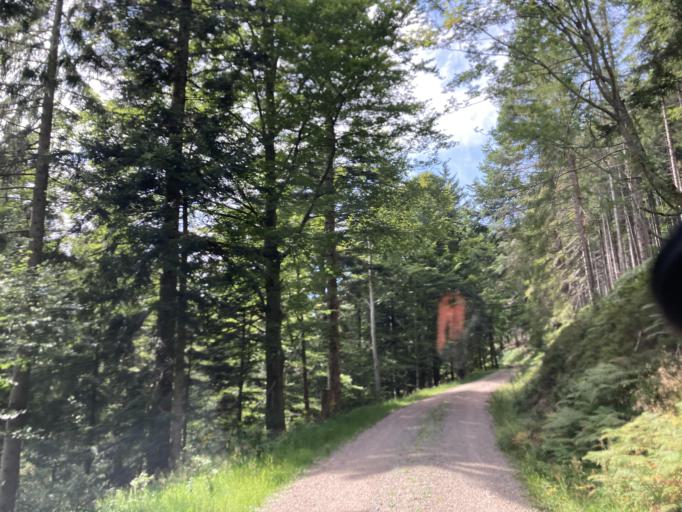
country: DE
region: Baden-Wuerttemberg
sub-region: Freiburg Region
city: Schonach im Schwarzwald
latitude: 48.1633
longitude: 8.1469
